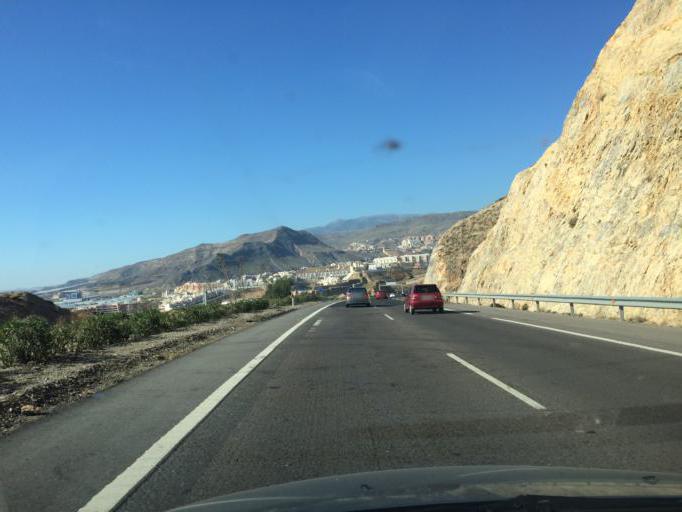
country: ES
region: Andalusia
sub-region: Provincia de Almeria
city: Aguadulce
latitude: 36.8220
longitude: -2.5718
